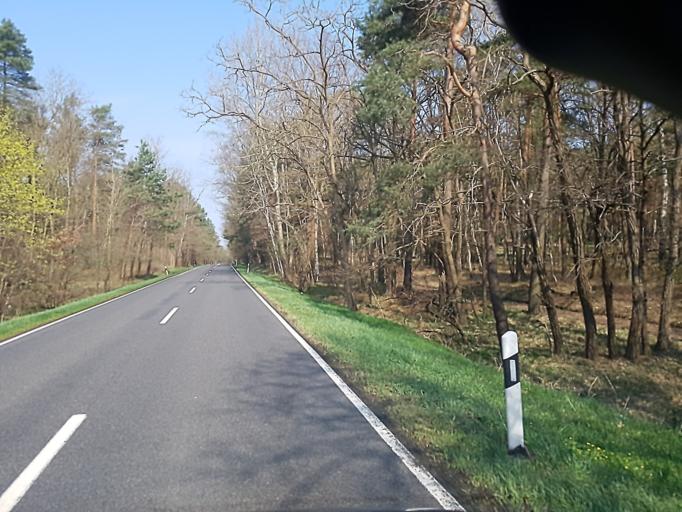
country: DE
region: Saxony-Anhalt
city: Radis
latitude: 51.6961
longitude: 12.5166
